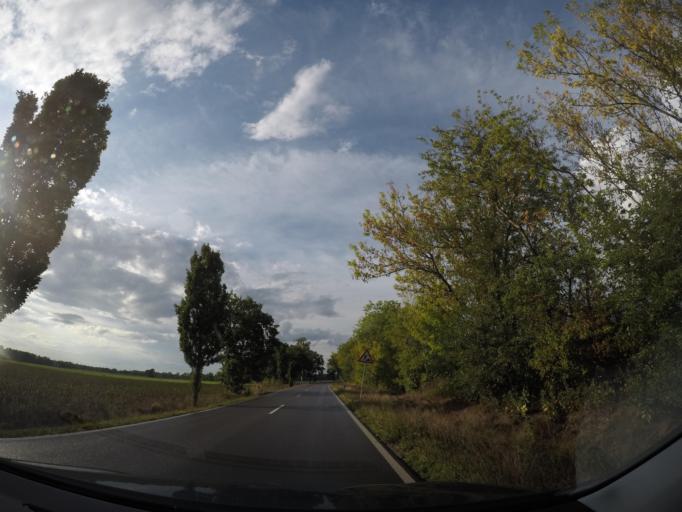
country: DE
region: Saxony-Anhalt
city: Kusey
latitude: 52.5416
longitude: 11.1451
